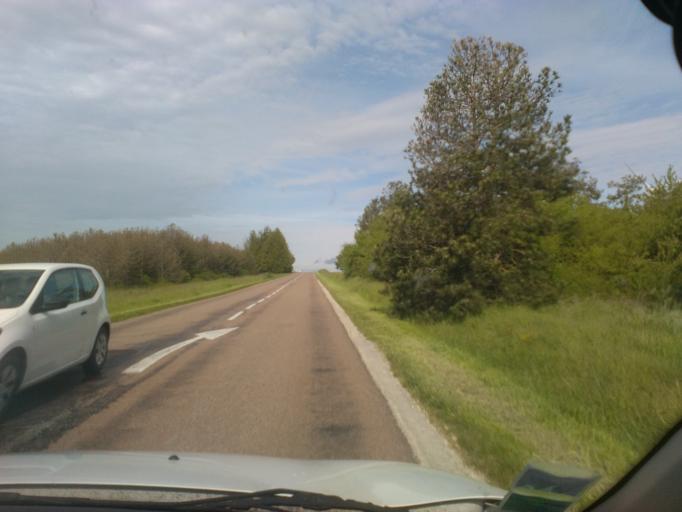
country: FR
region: Champagne-Ardenne
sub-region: Departement de l'Aube
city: Payns
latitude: 48.3660
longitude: 3.9300
